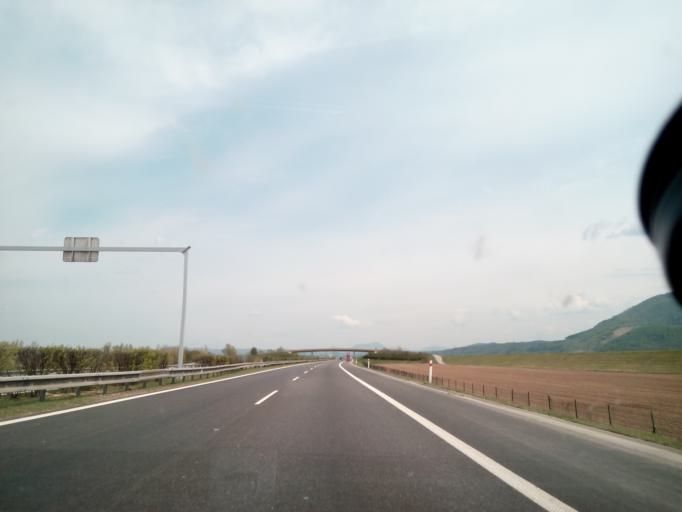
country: SK
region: Nitriansky
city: Ilava
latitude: 49.0142
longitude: 18.2478
